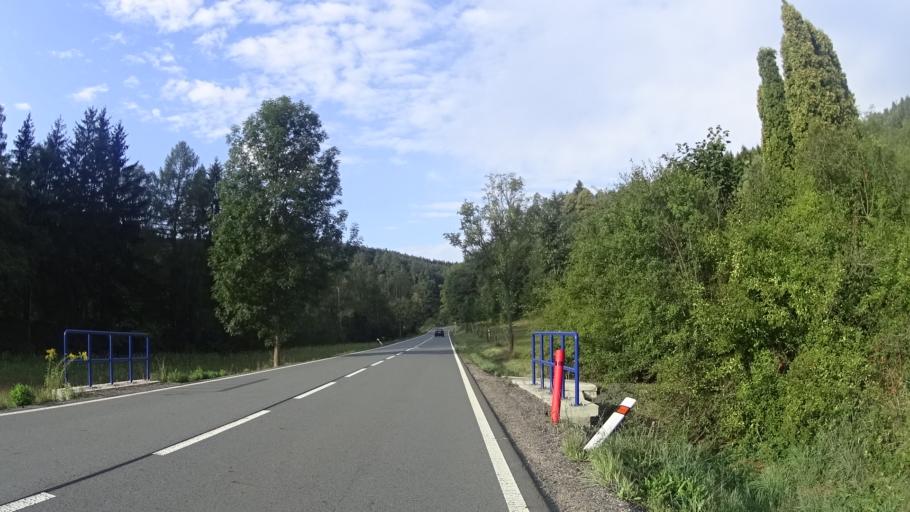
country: CZ
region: Olomoucky
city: Stity
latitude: 49.8662
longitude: 16.7268
